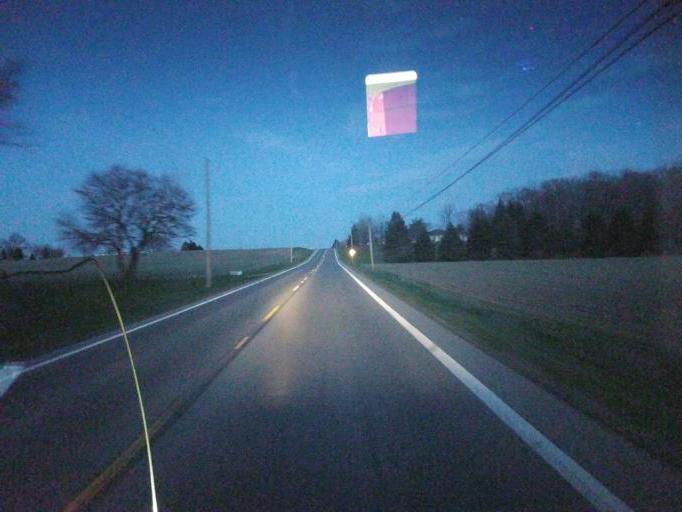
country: US
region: Ohio
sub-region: Logan County
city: Bellefontaine
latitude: 40.3662
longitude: -83.8439
